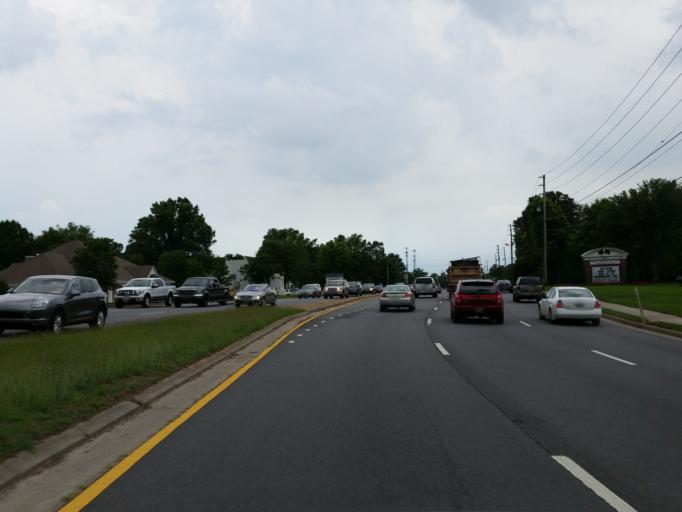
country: US
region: Georgia
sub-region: Fulton County
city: Sandy Springs
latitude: 33.9730
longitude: -84.4133
